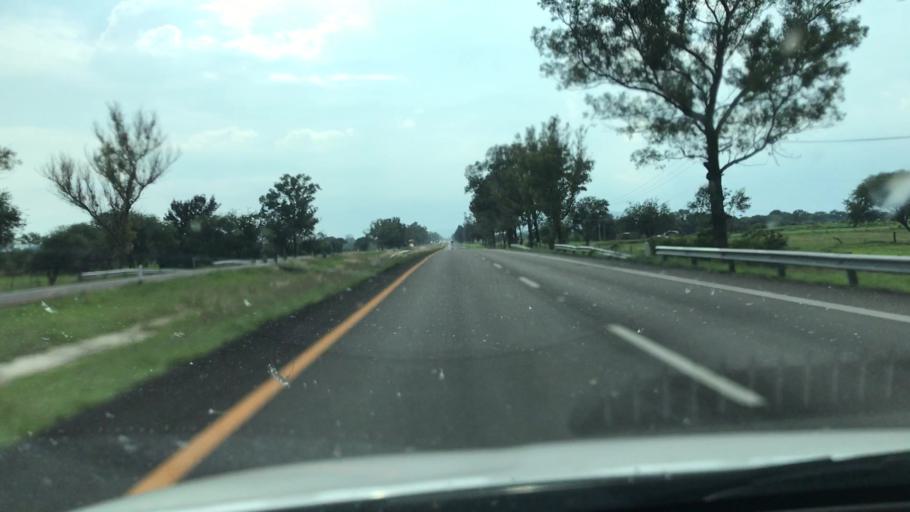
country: MX
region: Jalisco
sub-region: Ocotlan
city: Joconoxtle (La Tuna)
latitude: 20.3752
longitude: -102.6683
